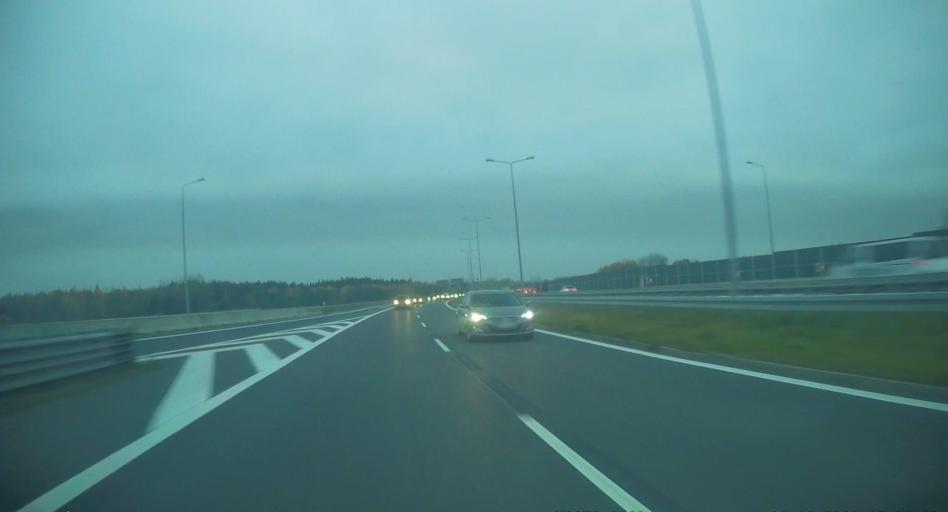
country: PL
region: Silesian Voivodeship
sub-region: Powiat tarnogorski
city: Ozarowice
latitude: 50.4525
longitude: 19.0768
